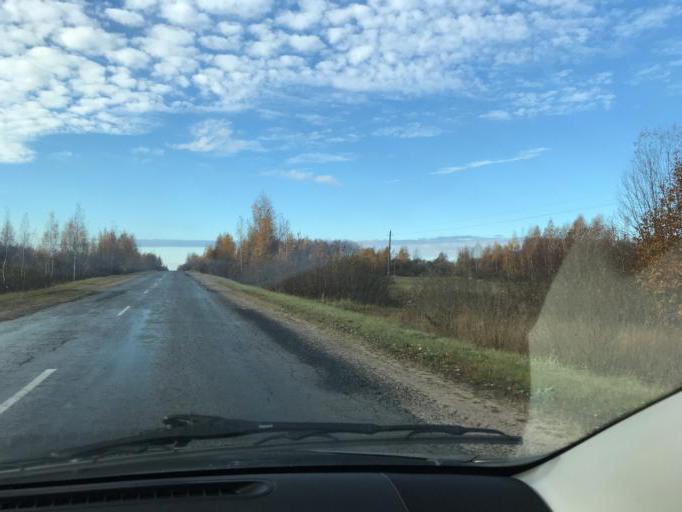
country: BY
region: Vitebsk
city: Haradok
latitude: 55.4182
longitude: 29.7819
